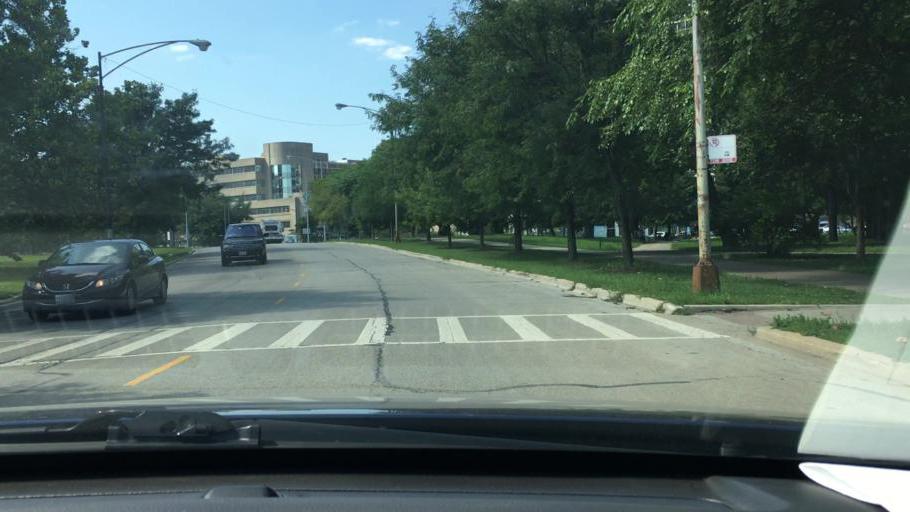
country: US
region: Illinois
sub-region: Cook County
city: Chicago
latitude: 41.9320
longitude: -87.6377
